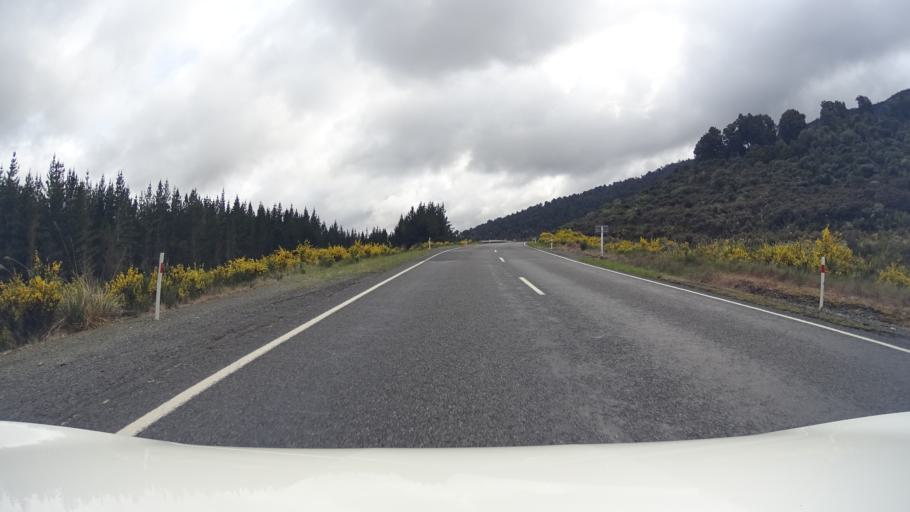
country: NZ
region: Manawatu-Wanganui
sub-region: Ruapehu District
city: Waiouru
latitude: -39.2239
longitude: 175.3975
